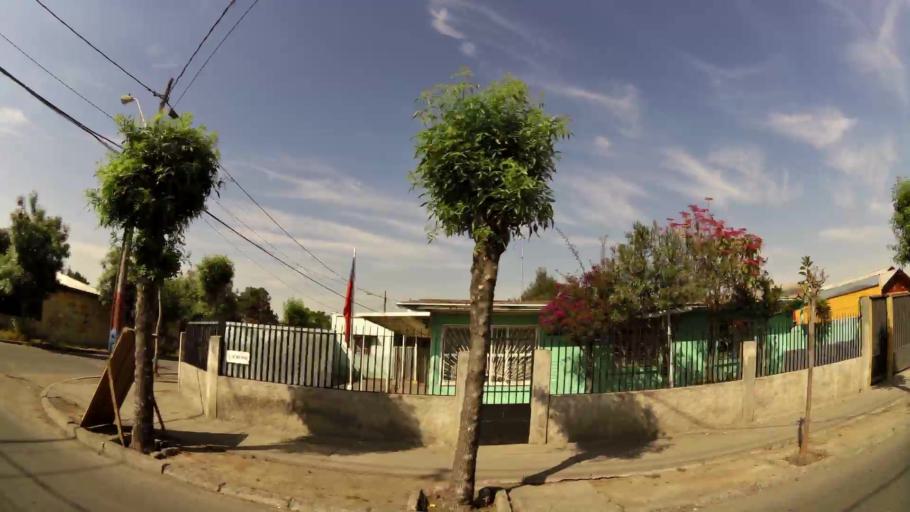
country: CL
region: Santiago Metropolitan
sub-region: Provincia de Santiago
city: La Pintana
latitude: -33.5629
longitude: -70.6666
